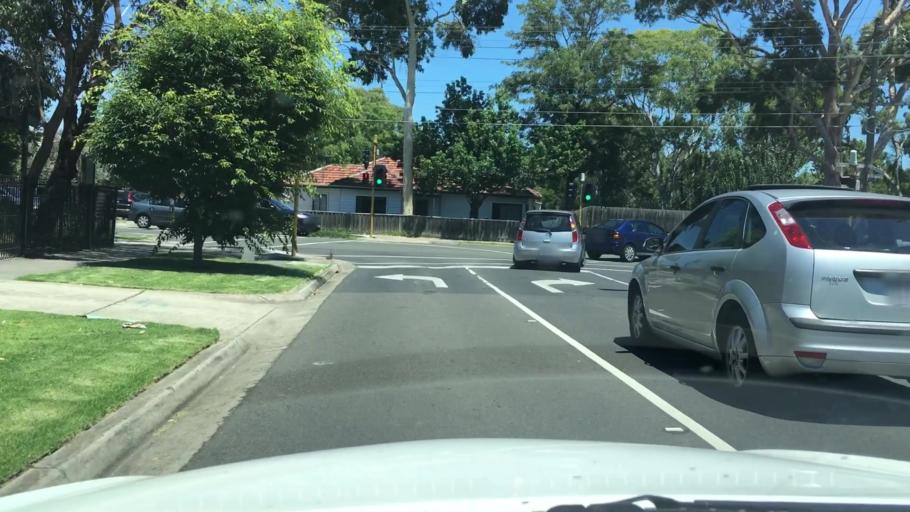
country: AU
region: Victoria
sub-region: Greater Dandenong
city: Noble Park
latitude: -37.9654
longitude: 145.1788
